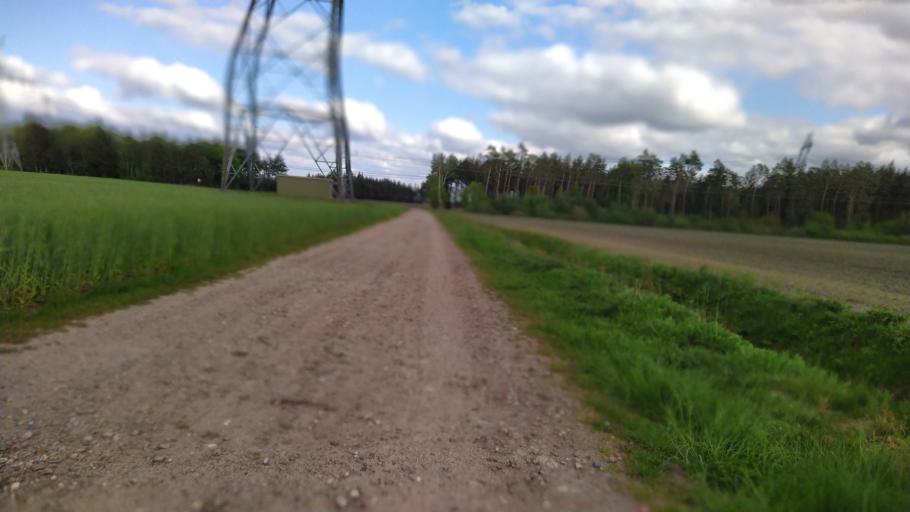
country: DE
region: Lower Saxony
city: Brest
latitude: 53.4345
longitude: 9.3911
